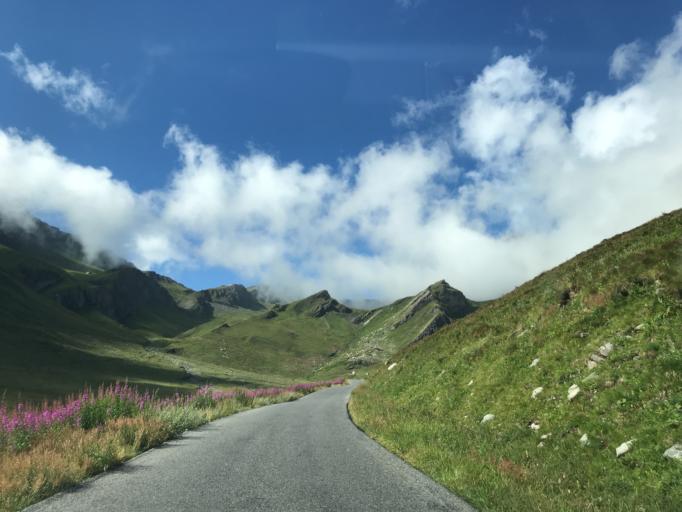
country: IT
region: Piedmont
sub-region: Provincia di Cuneo
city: Pontechianale
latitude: 44.6658
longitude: 6.9868
